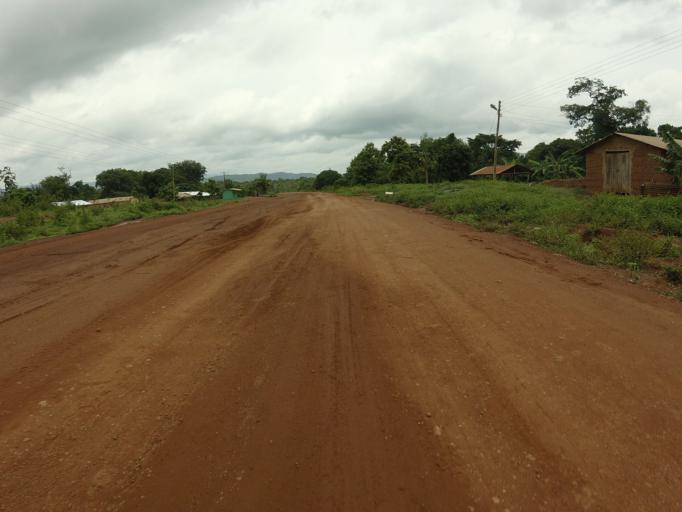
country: GH
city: Kpandae
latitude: 8.2993
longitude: 0.4867
